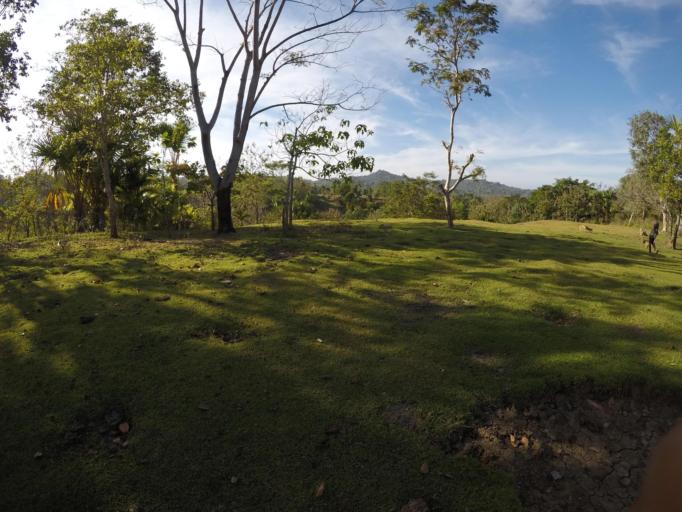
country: TL
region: Viqueque
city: Viqueque
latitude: -8.8338
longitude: 126.3783
